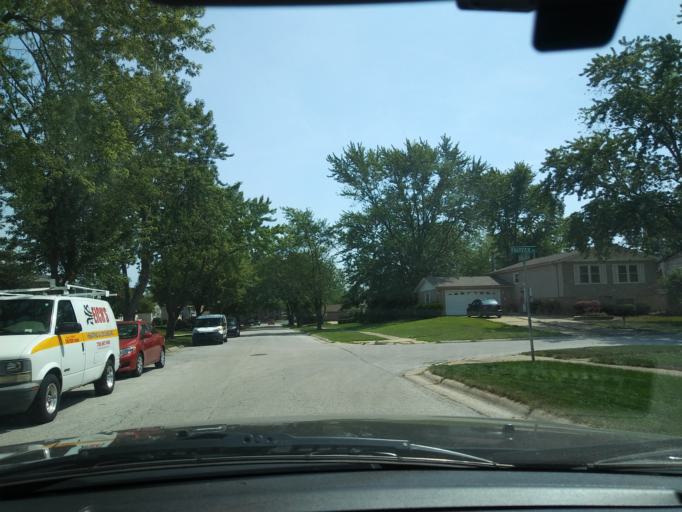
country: US
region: Illinois
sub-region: Cook County
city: Oak Forest
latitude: 41.6097
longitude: -87.7569
